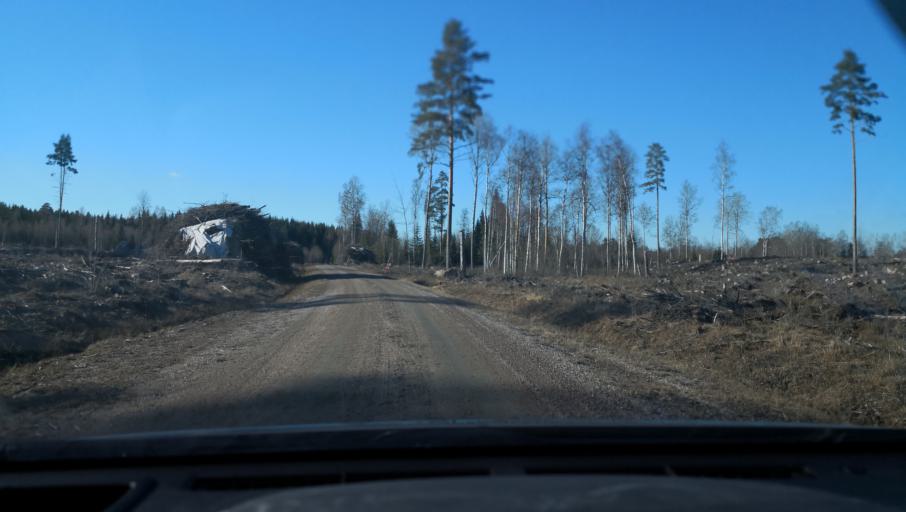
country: SE
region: Dalarna
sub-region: Avesta Kommun
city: Horndal
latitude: 60.1766
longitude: 16.6311
